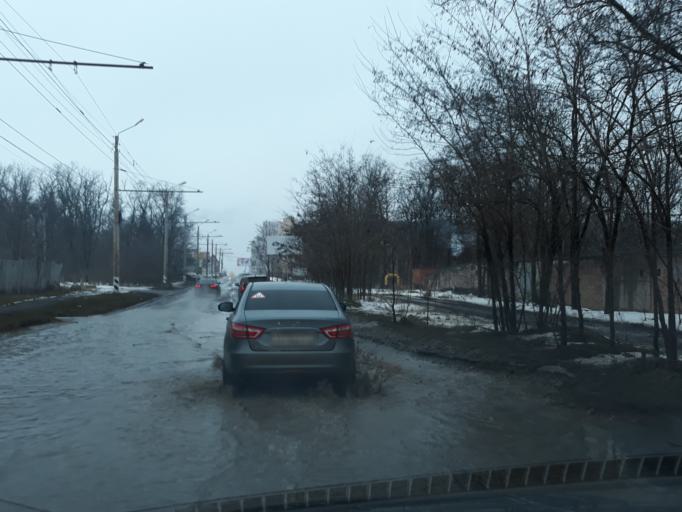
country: RU
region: Rostov
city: Taganrog
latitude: 47.2782
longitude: 38.9207
